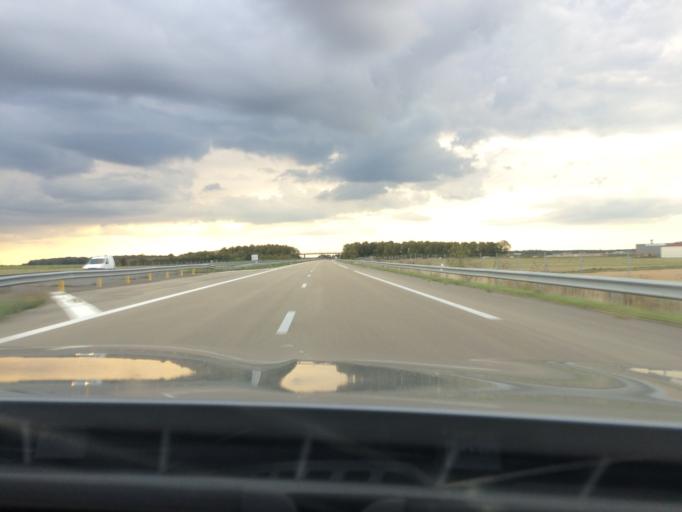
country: FR
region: Ile-de-France
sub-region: Departement de Seine-et-Marne
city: Egreville
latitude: 48.1931
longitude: 2.8140
